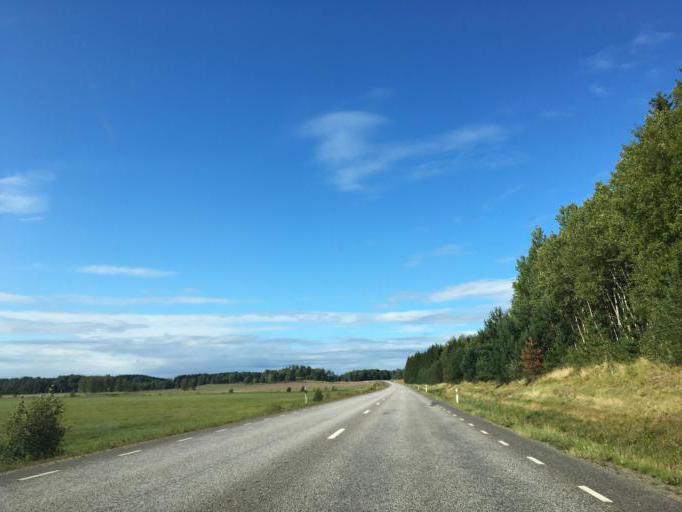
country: SE
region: Soedermanland
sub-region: Nykopings Kommun
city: Nykoping
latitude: 58.7934
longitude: 16.9549
